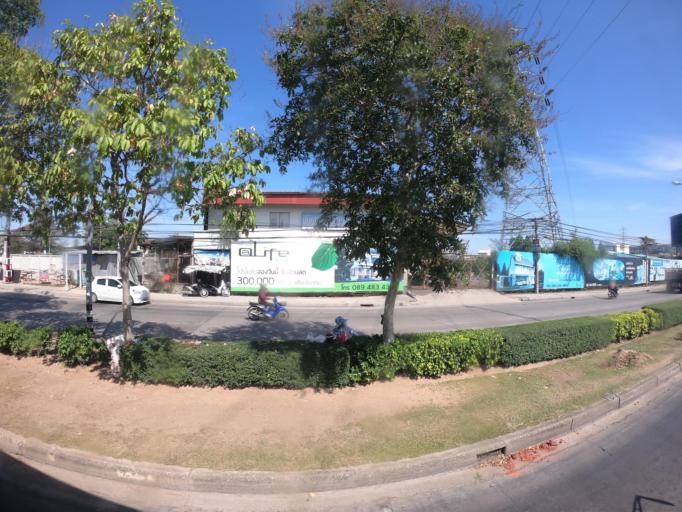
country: TH
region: Nakhon Ratchasima
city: Nakhon Ratchasima
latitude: 14.9951
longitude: 102.1025
